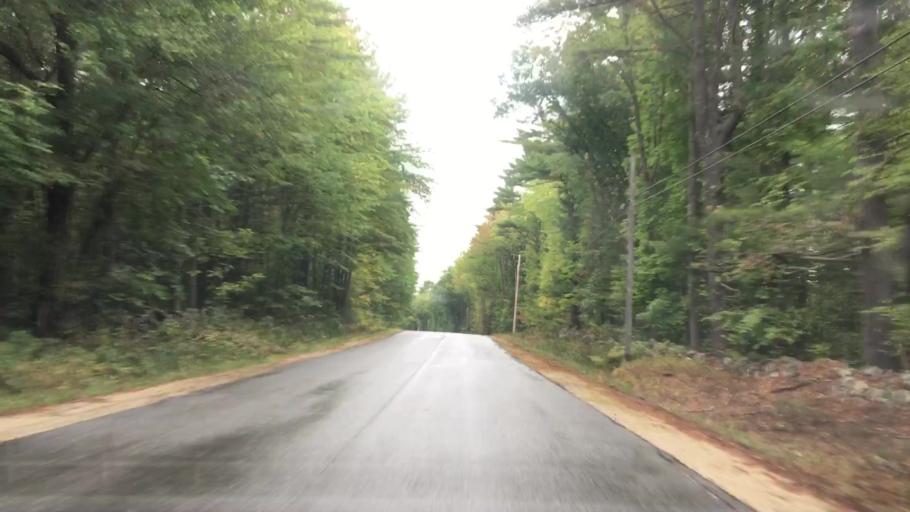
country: US
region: Maine
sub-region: Cumberland County
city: Harrison
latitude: 44.0439
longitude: -70.6122
